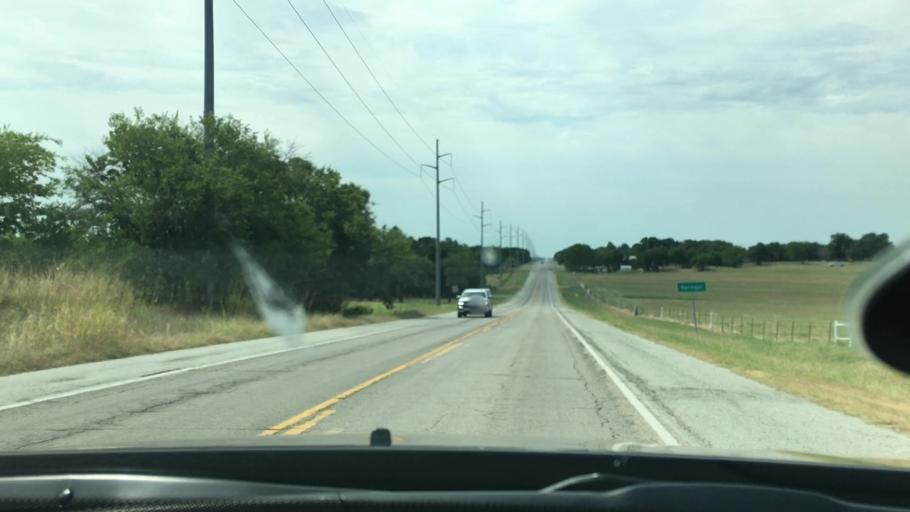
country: US
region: Oklahoma
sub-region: Carter County
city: Ardmore
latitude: 34.3204
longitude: -97.1430
